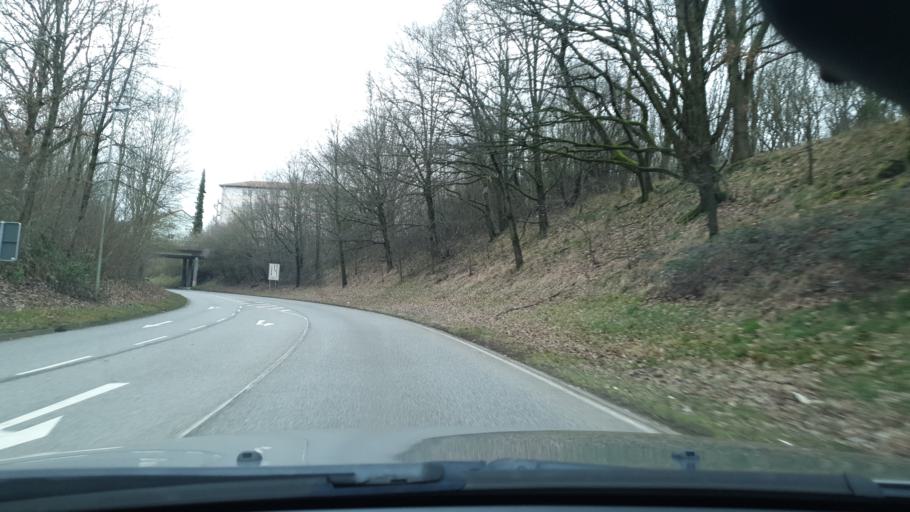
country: DE
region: Rheinland-Pfalz
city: Zweibrucken
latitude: 49.2580
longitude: 7.3808
